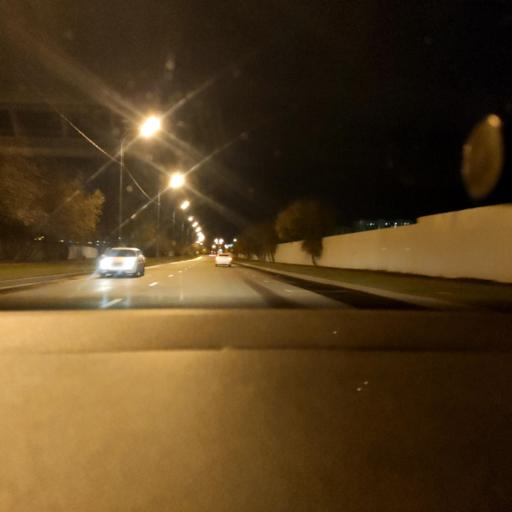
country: RU
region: Moscow
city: Kuz'minki
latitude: 55.6774
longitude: 37.7870
